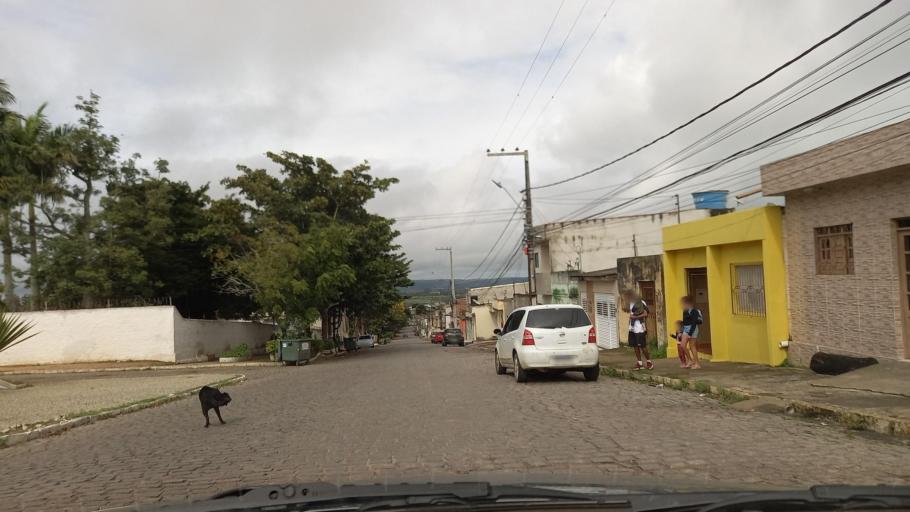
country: BR
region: Pernambuco
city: Garanhuns
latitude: -8.9018
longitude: -36.4943
